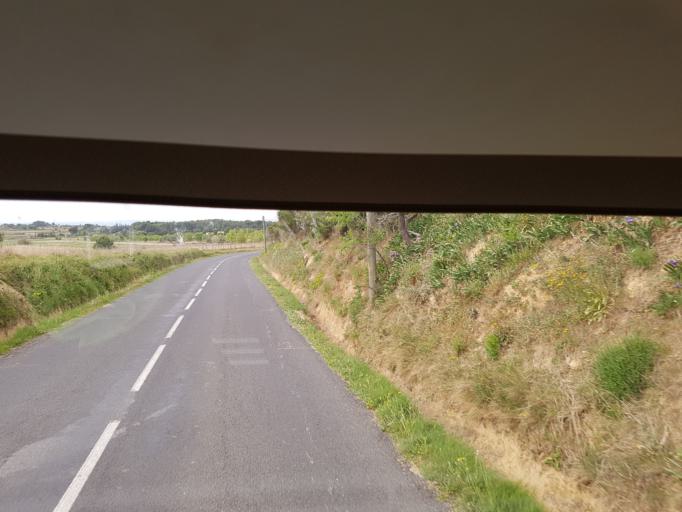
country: FR
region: Languedoc-Roussillon
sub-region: Departement de l'Aude
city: Fleury
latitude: 43.2141
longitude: 3.1341
